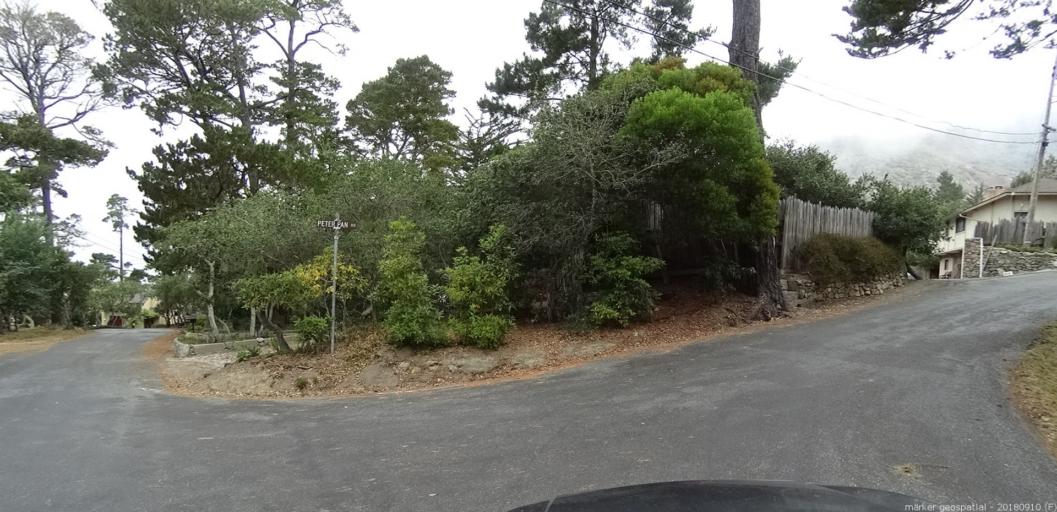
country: US
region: California
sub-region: Monterey County
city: Carmel-by-the-Sea
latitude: 36.4952
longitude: -121.9338
